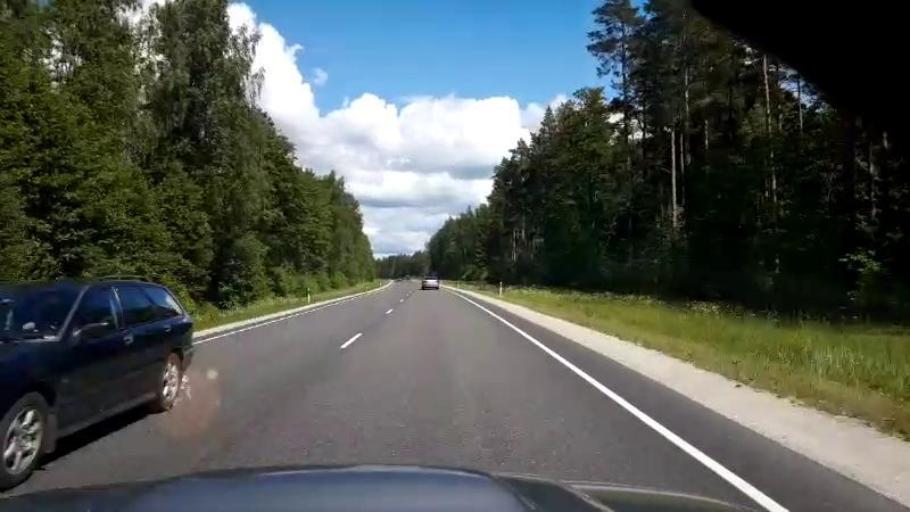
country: EE
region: Paernumaa
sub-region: Paernu linn
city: Parnu
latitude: 58.2608
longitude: 24.5445
